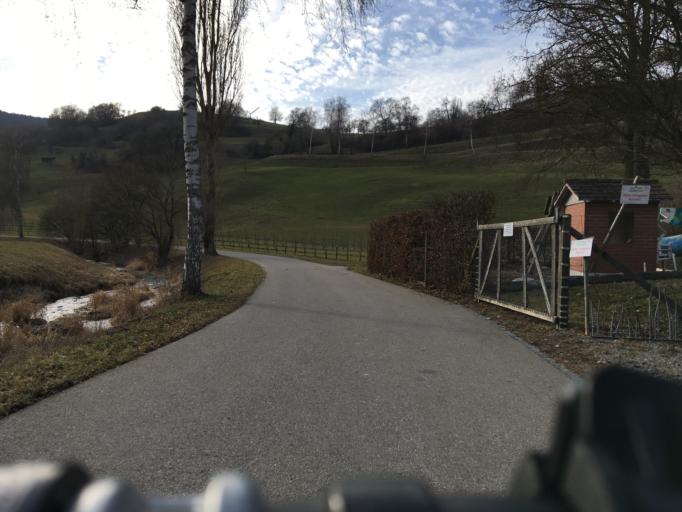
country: CH
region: Schaffhausen
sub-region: Bezirk Reiat
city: Stetten
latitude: 47.7781
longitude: 8.6702
